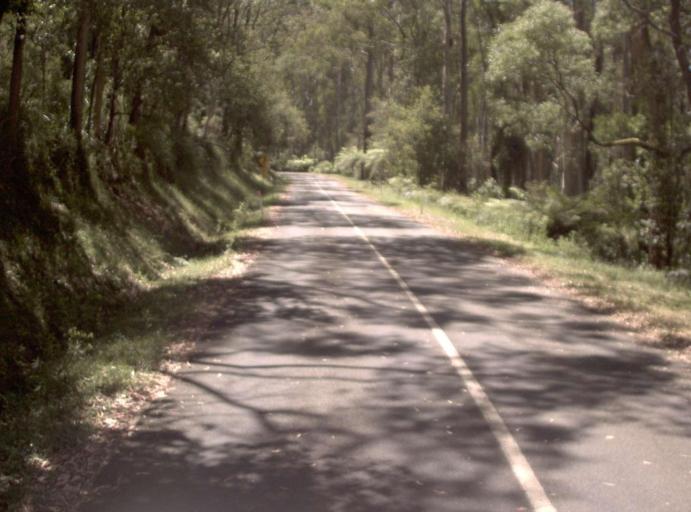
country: AU
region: Victoria
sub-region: Yarra Ranges
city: Millgrove
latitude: -37.7414
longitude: 145.7207
